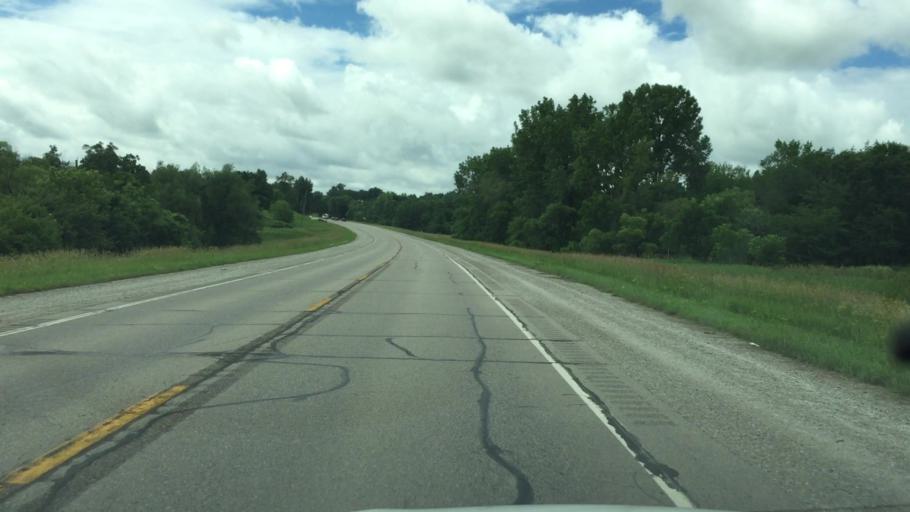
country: US
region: Iowa
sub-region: Jasper County
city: Monroe
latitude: 41.5363
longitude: -93.1012
